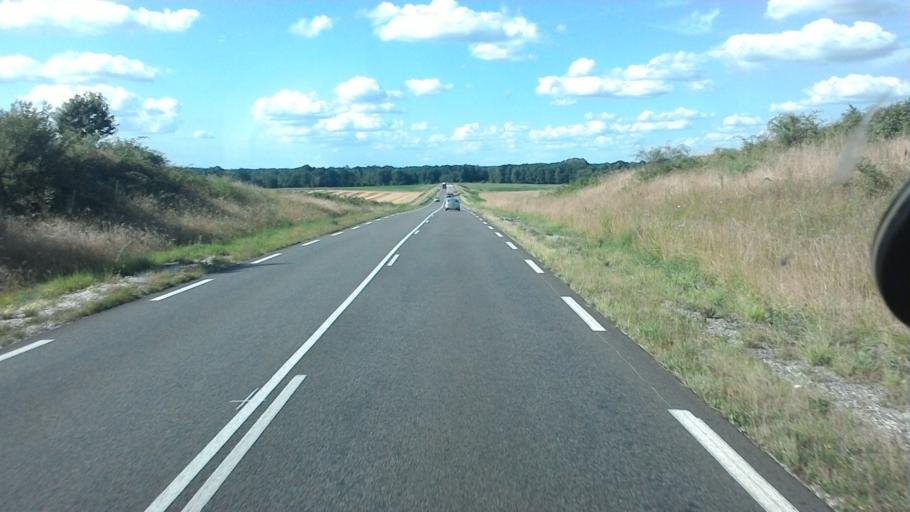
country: FR
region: Franche-Comte
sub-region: Departement de la Haute-Saone
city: Rioz
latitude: 47.4855
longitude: 5.9357
